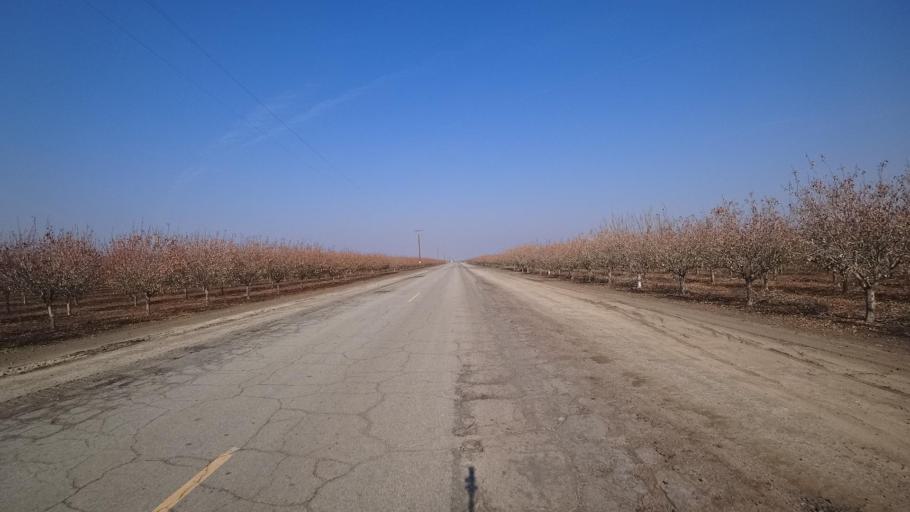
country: US
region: California
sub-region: Kern County
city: Buttonwillow
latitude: 35.3431
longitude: -119.3945
